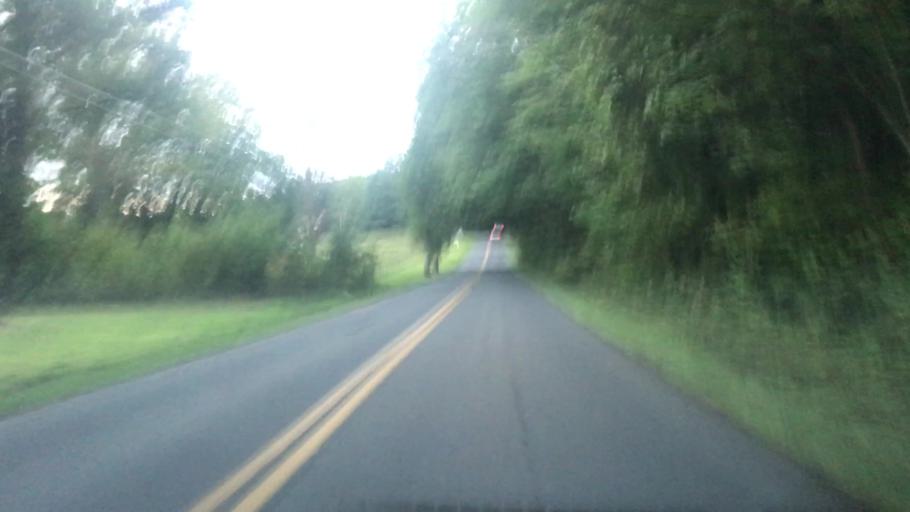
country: US
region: Virginia
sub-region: Prince William County
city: Nokesville
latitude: 38.6952
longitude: -77.6687
